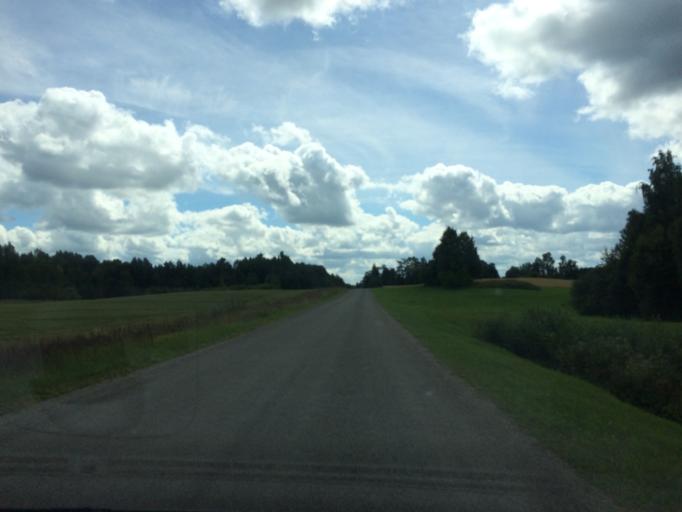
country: LV
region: Ludzas Rajons
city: Ludza
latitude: 56.6432
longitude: 27.5119
